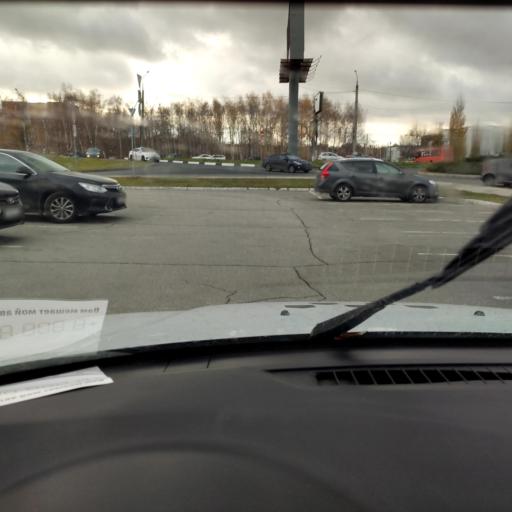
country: RU
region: Samara
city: Tol'yatti
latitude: 53.5392
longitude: 49.3883
